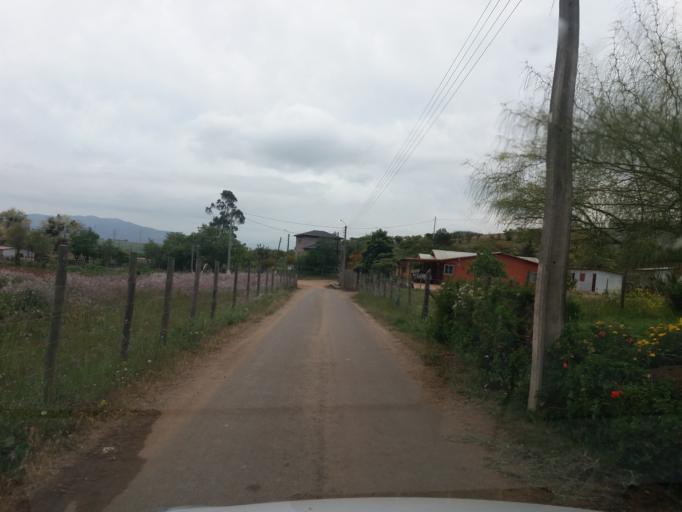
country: CL
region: Valparaiso
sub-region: Provincia de Quillota
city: Quillota
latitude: -32.8956
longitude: -71.3202
